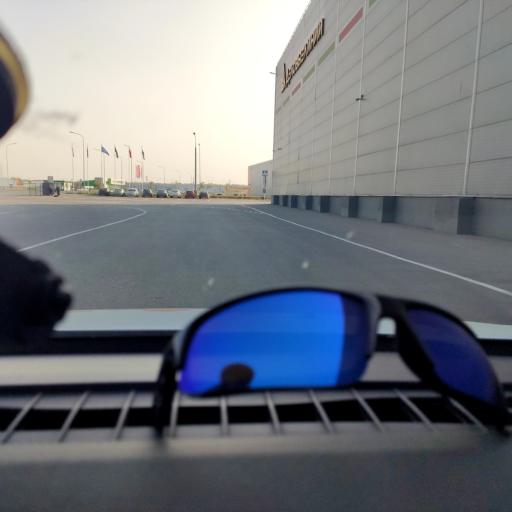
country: RU
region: Samara
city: Samara
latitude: 53.0945
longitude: 50.1341
